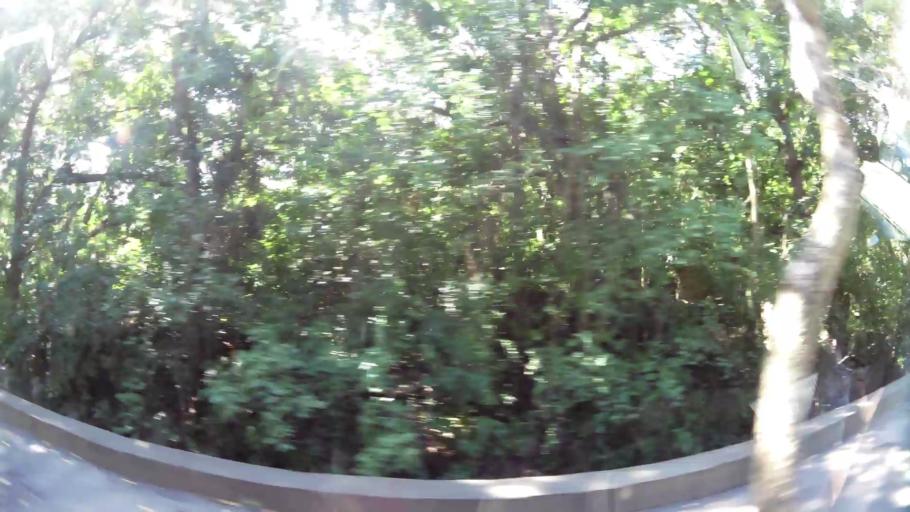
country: VG
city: Road Town
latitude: 18.4321
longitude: -64.6251
